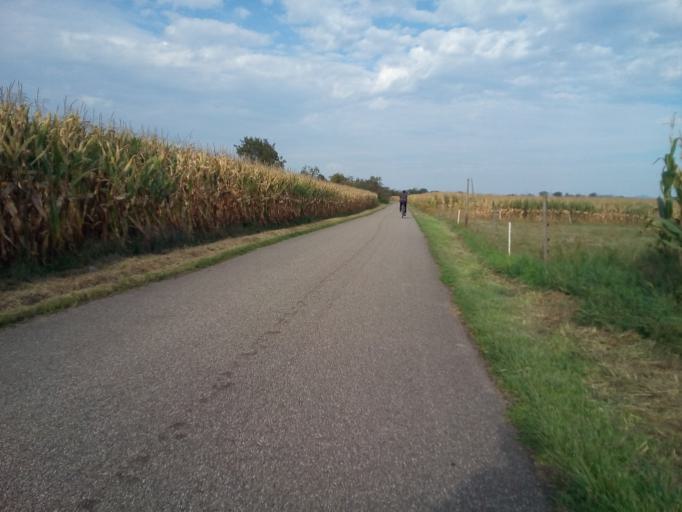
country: DE
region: Baden-Wuerttemberg
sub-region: Freiburg Region
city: Rheinau
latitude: 48.6749
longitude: 7.9463
